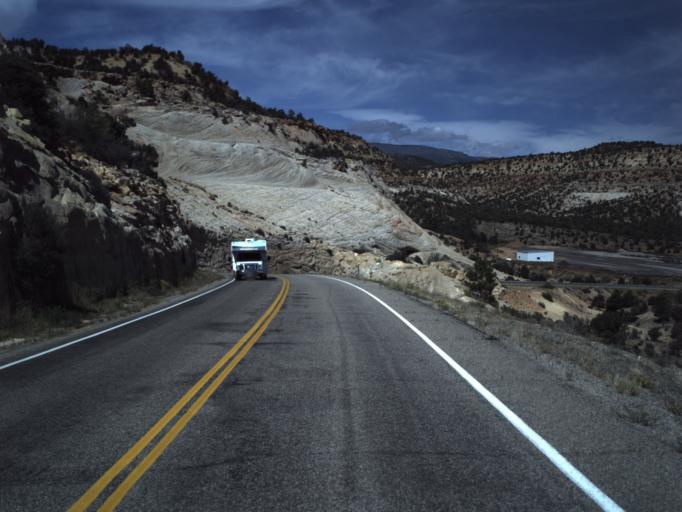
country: US
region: Utah
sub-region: Wayne County
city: Loa
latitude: 37.8938
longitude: -111.4468
